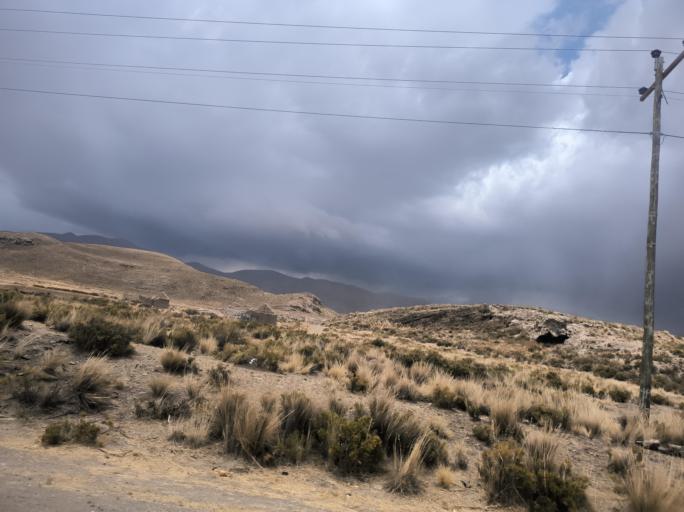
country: BO
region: Oruro
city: Challapata
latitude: -18.7558
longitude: -66.8619
